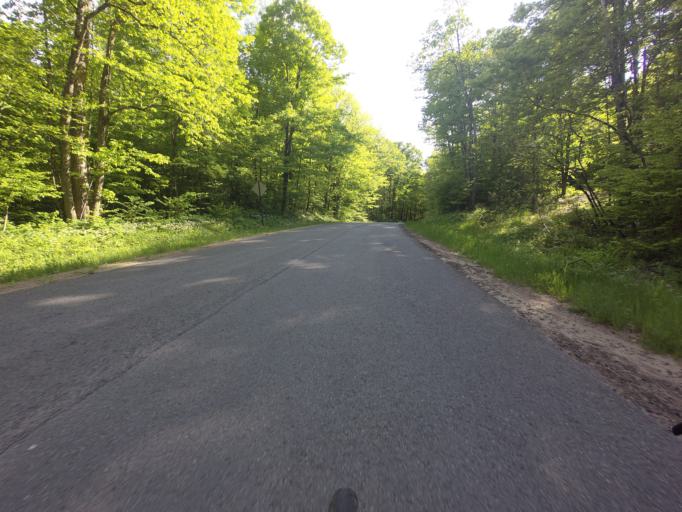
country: US
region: New York
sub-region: St. Lawrence County
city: Gouverneur
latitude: 44.2049
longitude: -75.2524
